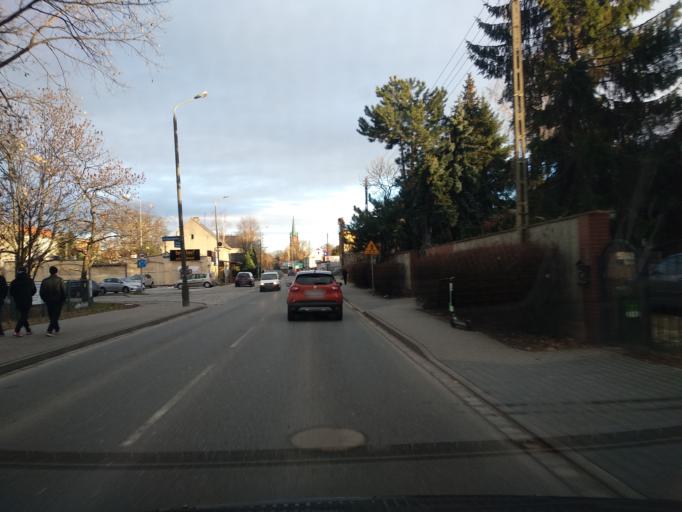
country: PL
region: Lower Silesian Voivodeship
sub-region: Powiat wroclawski
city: Wroclaw
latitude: 51.0581
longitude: 17.0165
